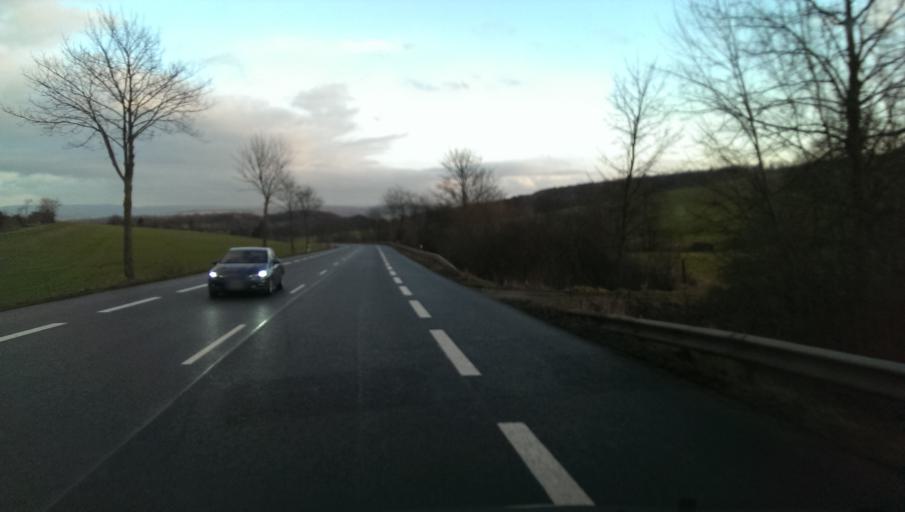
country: DE
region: Lower Saxony
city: Kreiensen
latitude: 51.8646
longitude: 9.9079
